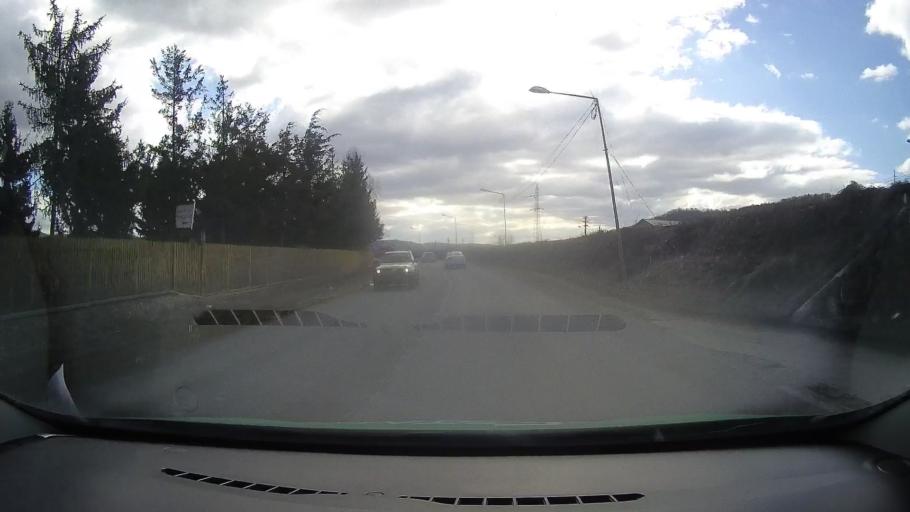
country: RO
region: Dambovita
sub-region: Oras Pucioasa
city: Pucioasa
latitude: 45.0845
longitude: 25.4215
